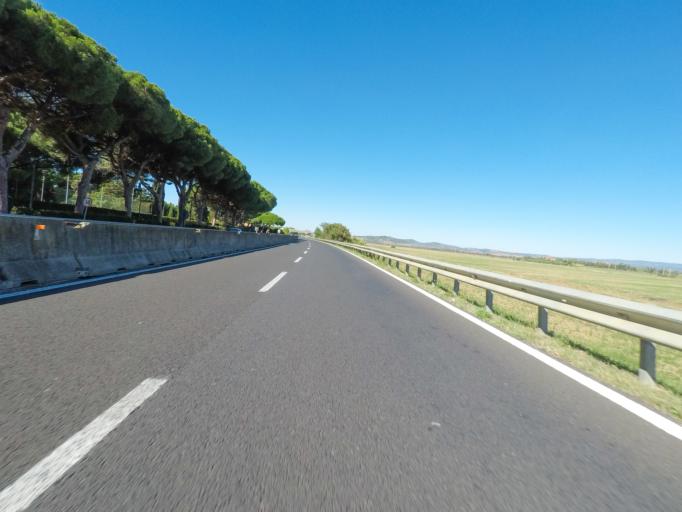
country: IT
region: Tuscany
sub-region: Provincia di Grosseto
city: Albinia
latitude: 42.5195
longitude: 11.1931
